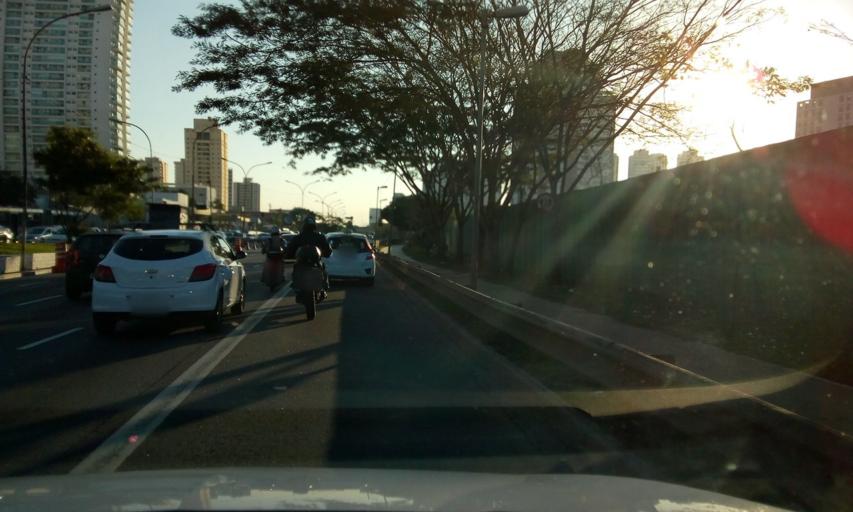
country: BR
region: Sao Paulo
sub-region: Sao Paulo
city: Sao Paulo
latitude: -23.5384
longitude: -46.5661
